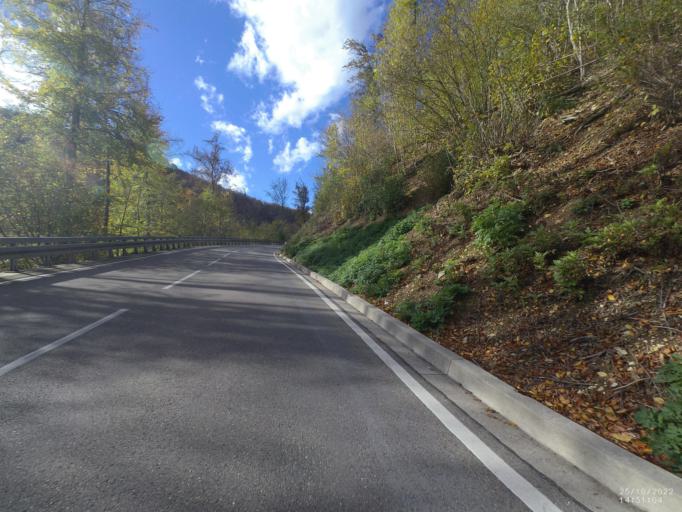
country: DE
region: Baden-Wuerttemberg
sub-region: Regierungsbezirk Stuttgart
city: Bohmenkirch
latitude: 48.6562
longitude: 9.8978
